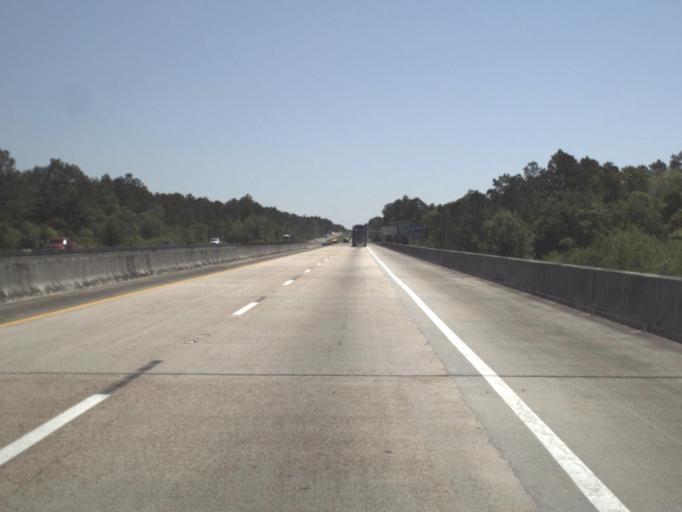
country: US
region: Florida
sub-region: Escambia County
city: Cantonment
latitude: 30.5736
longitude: -87.4126
